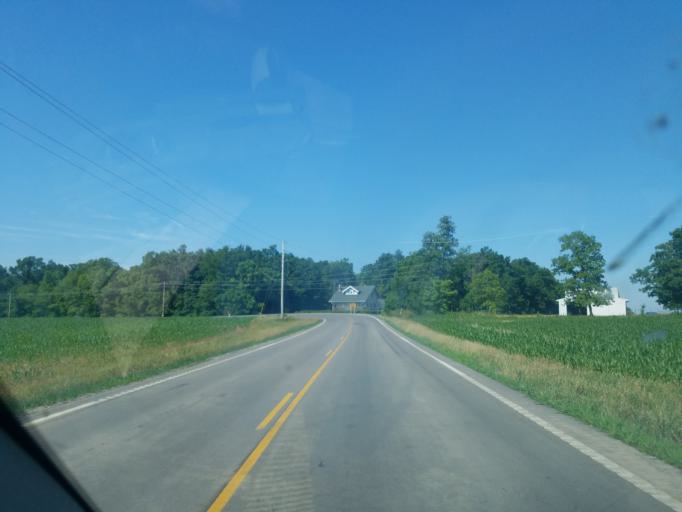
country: US
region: Ohio
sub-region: Logan County
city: Northwood
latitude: 40.4429
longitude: -83.7809
